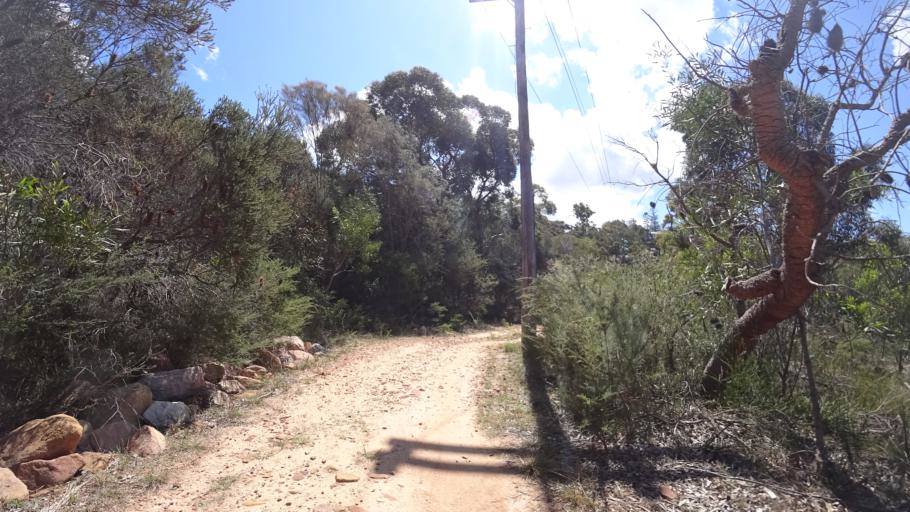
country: AU
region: New South Wales
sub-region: Warringah
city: Killarney Heights
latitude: -33.7631
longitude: 151.2220
